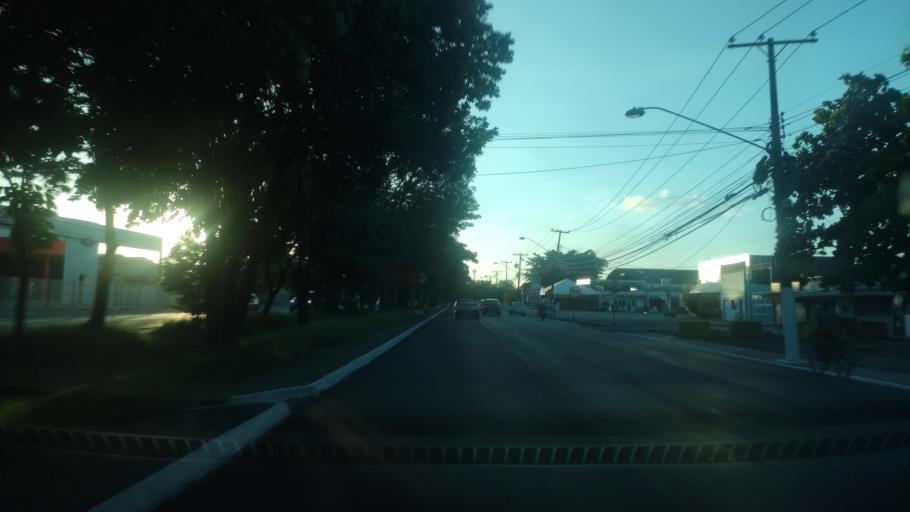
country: BR
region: Alagoas
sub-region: Satuba
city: Satuba
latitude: -9.5916
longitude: -35.7577
